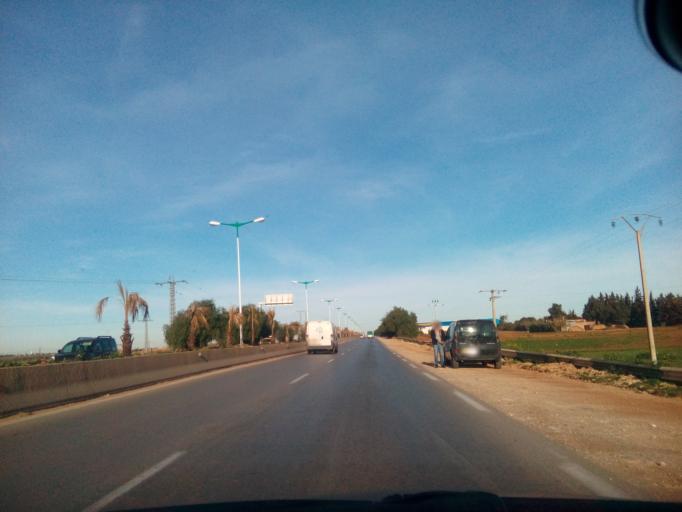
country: DZ
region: Mostaganem
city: Mostaganem
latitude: 35.8556
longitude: 0.1648
